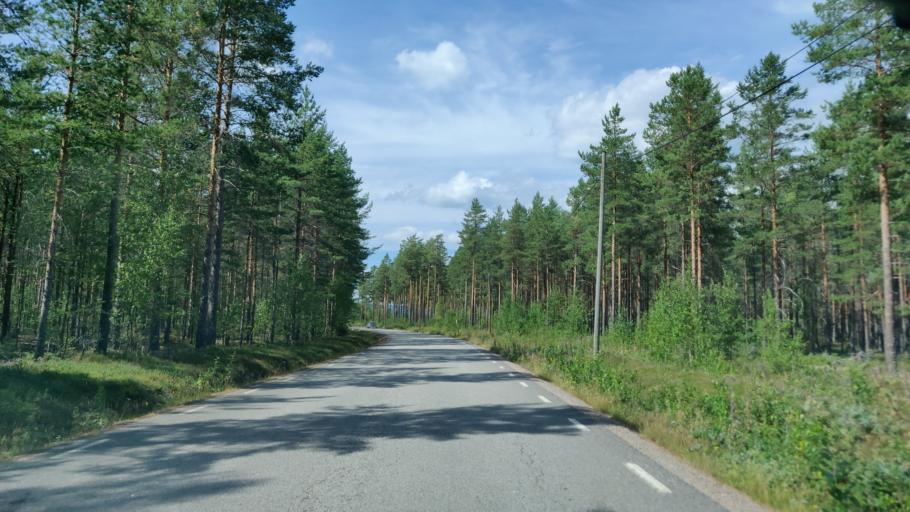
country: SE
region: Vaermland
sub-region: Hagfors Kommun
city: Ekshaerad
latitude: 60.0721
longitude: 13.5321
